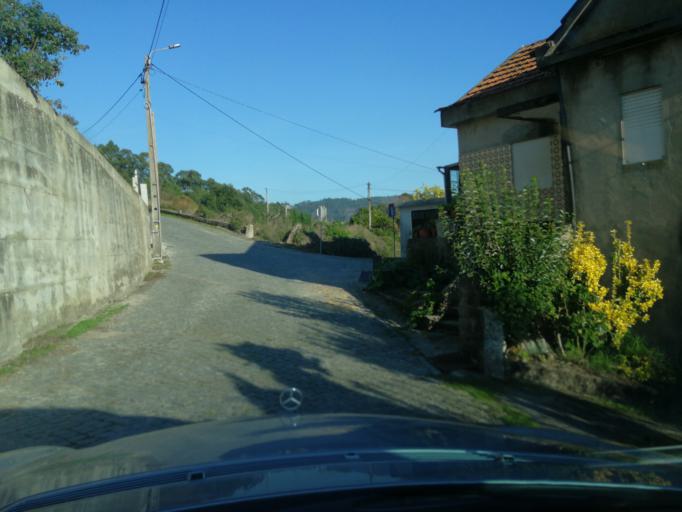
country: PT
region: Braga
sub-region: Braga
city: Oliveira
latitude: 41.4535
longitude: -8.4670
